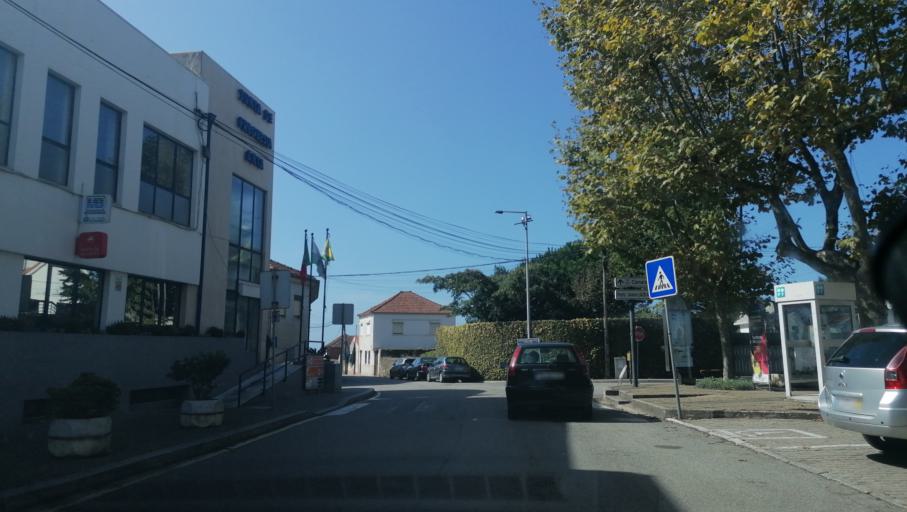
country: PT
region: Aveiro
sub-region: Espinho
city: Silvalde
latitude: 41.0060
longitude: -8.6249
